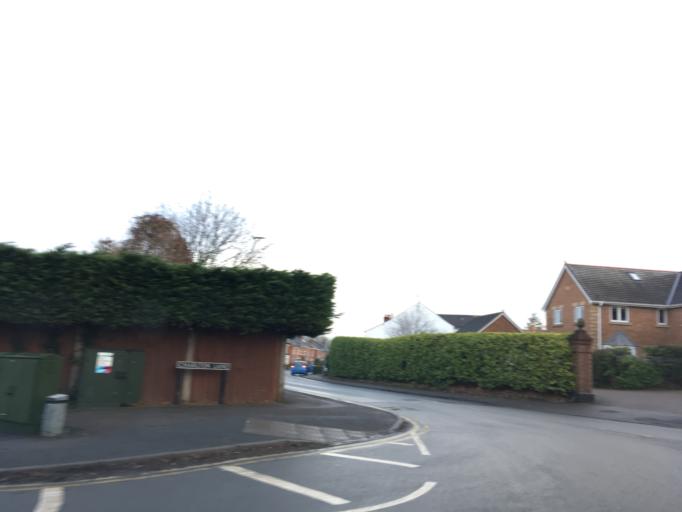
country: GB
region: England
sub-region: Gloucestershire
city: Cheltenham
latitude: 51.8779
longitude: -2.0771
